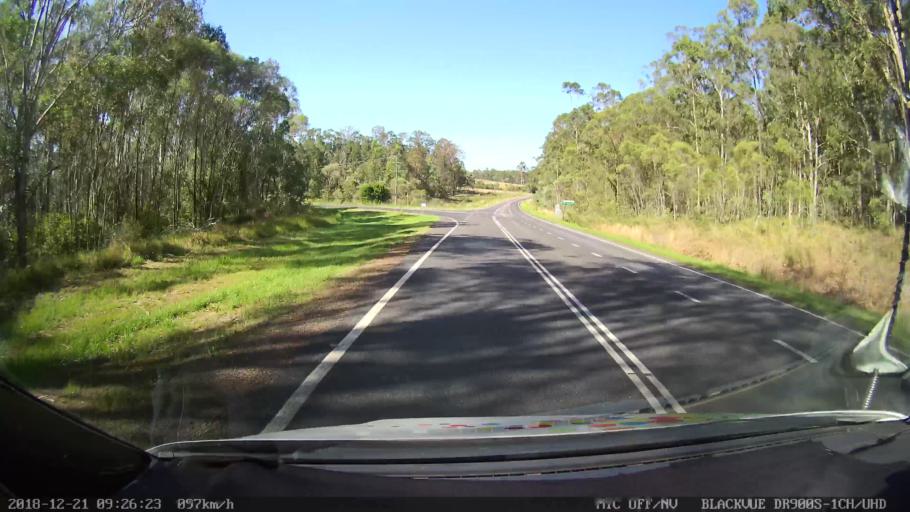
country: AU
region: New South Wales
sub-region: Clarence Valley
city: Maclean
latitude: -29.3924
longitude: 153.0029
